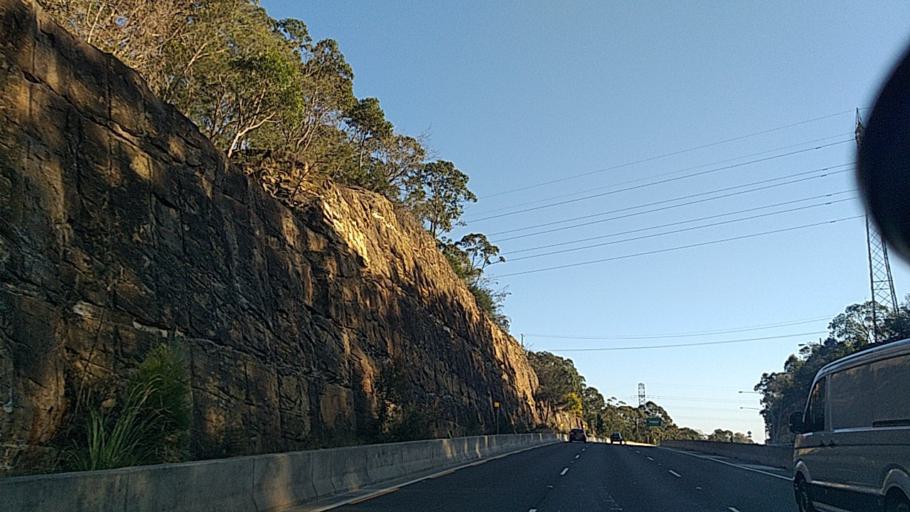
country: AU
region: New South Wales
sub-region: Bankstown
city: Padstow
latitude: -33.9714
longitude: 151.0318
